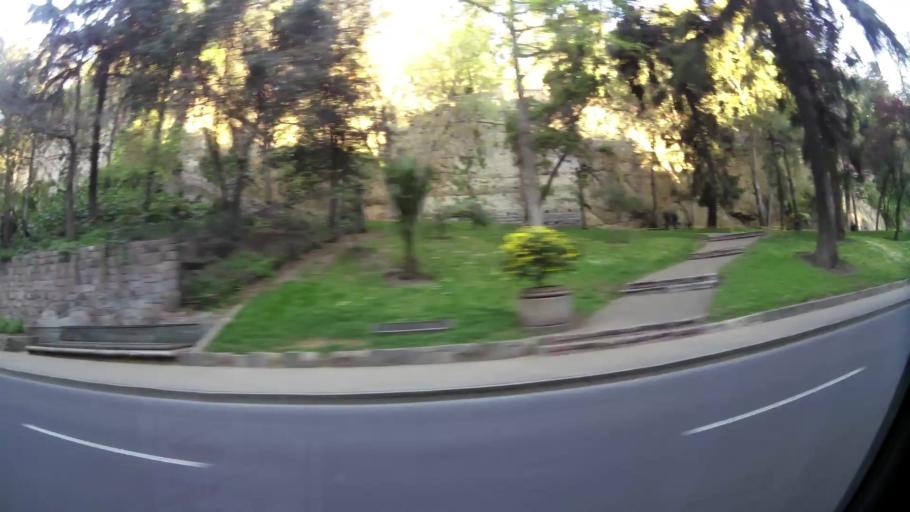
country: CL
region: Santiago Metropolitan
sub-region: Provincia de Santiago
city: Santiago
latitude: -33.4392
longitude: -70.6442
